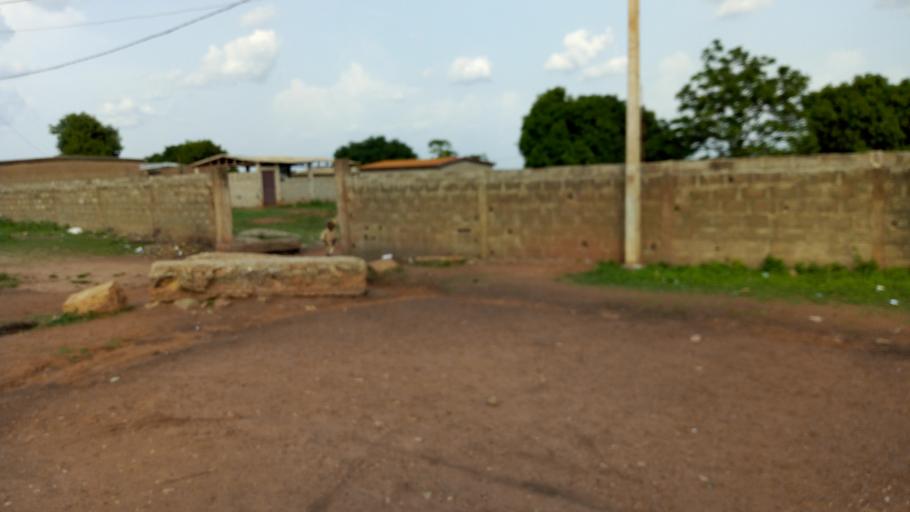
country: CI
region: Vallee du Bandama
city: Bouake
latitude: 7.7278
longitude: -5.0413
